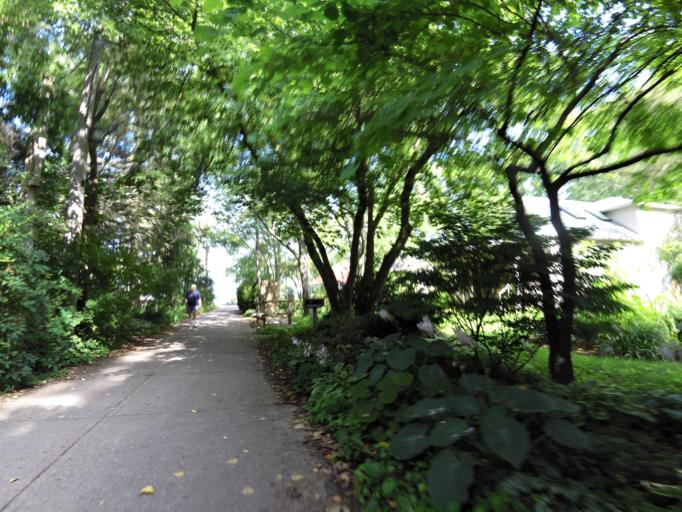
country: CA
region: Ontario
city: Toronto
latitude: 43.6291
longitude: -79.3586
